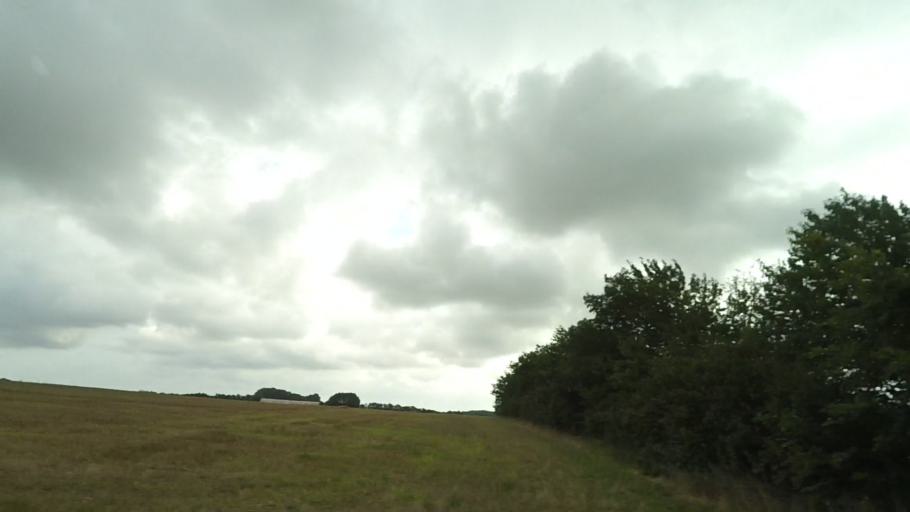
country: DK
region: Central Jutland
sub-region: Syddjurs Kommune
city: Ryomgard
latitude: 56.3911
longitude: 10.5651
